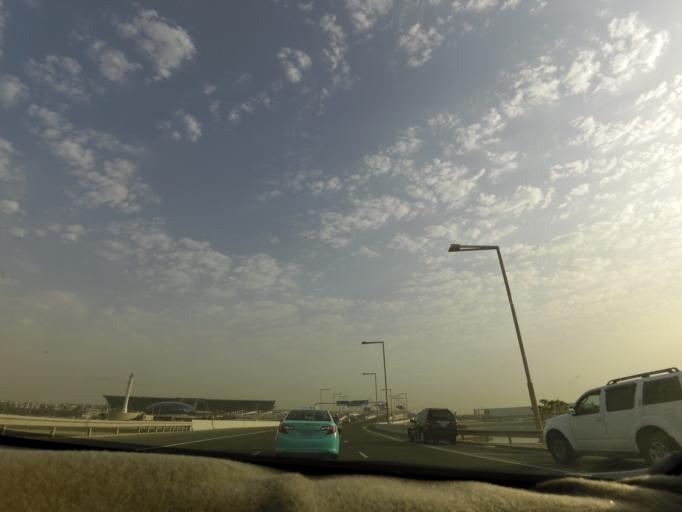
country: QA
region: Al Wakrah
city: Al Wakrah
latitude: 25.2558
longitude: 51.6172
